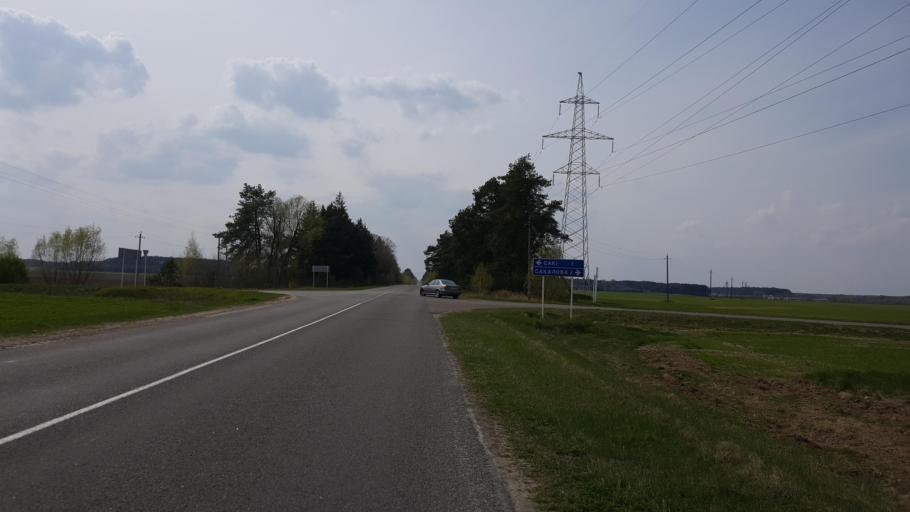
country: BY
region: Brest
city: Zhabinka
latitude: 52.2092
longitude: 23.9464
